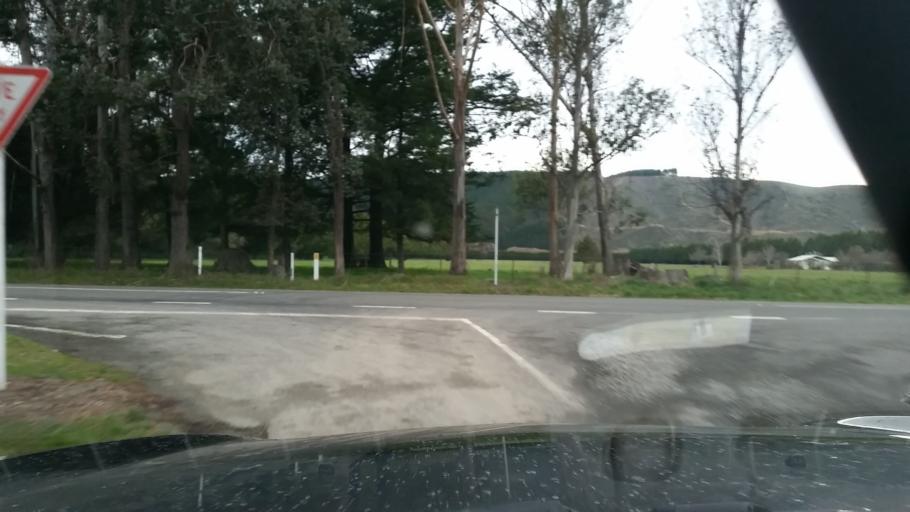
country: NZ
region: Nelson
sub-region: Nelson City
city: Nelson
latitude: -41.5668
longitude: 173.5250
